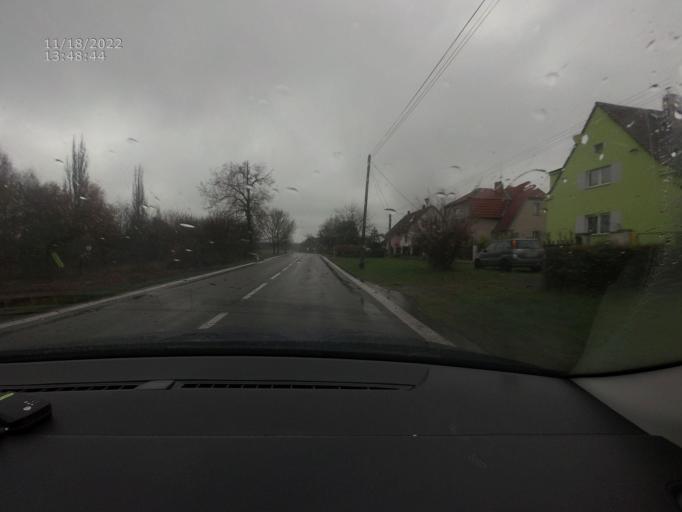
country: CZ
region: Jihocesky
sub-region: Okres Strakonice
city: Blatna
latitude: 49.4167
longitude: 13.8867
